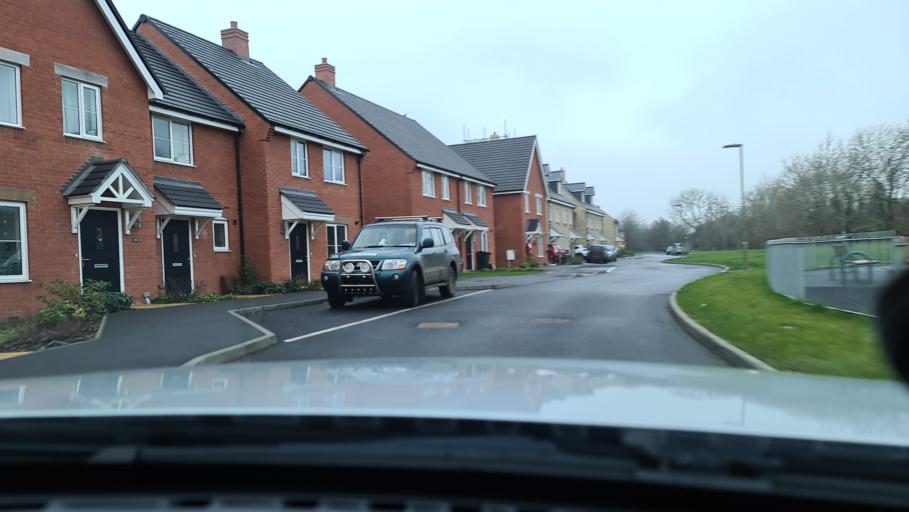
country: GB
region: England
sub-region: Oxfordshire
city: Bicester
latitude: 51.9075
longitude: -1.1316
